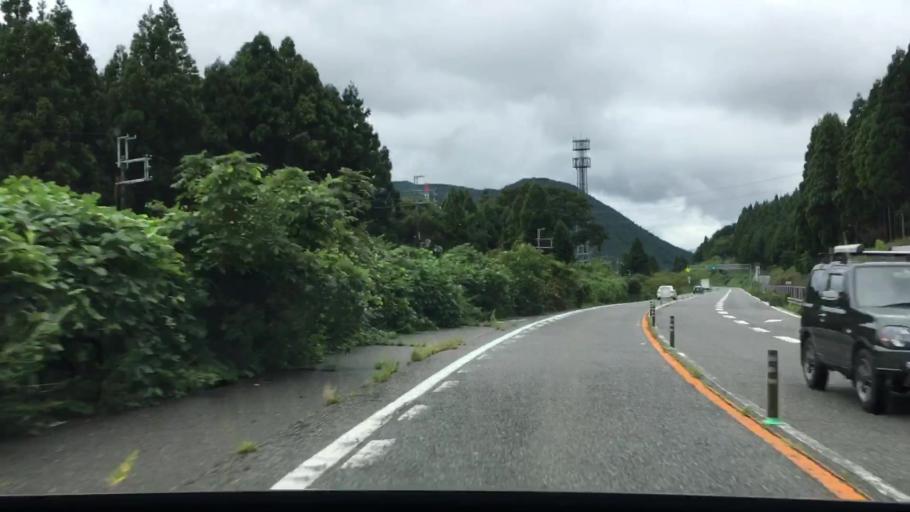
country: JP
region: Hyogo
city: Nishiwaki
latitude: 35.1244
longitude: 134.7874
